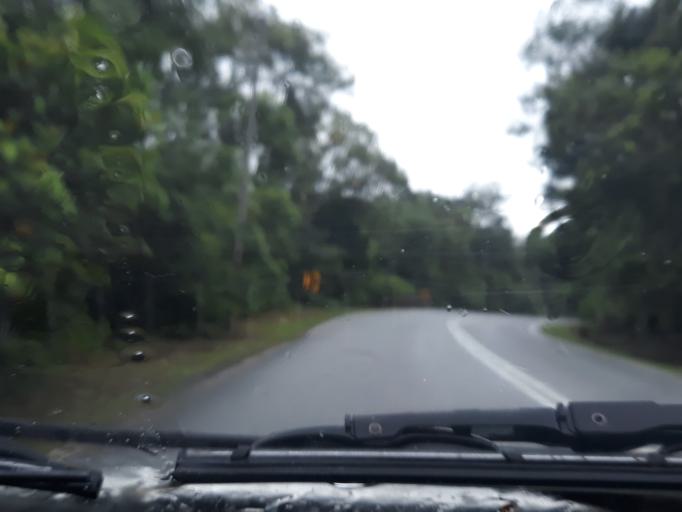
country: MY
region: Kedah
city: Kulim
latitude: 5.2781
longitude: 100.6195
